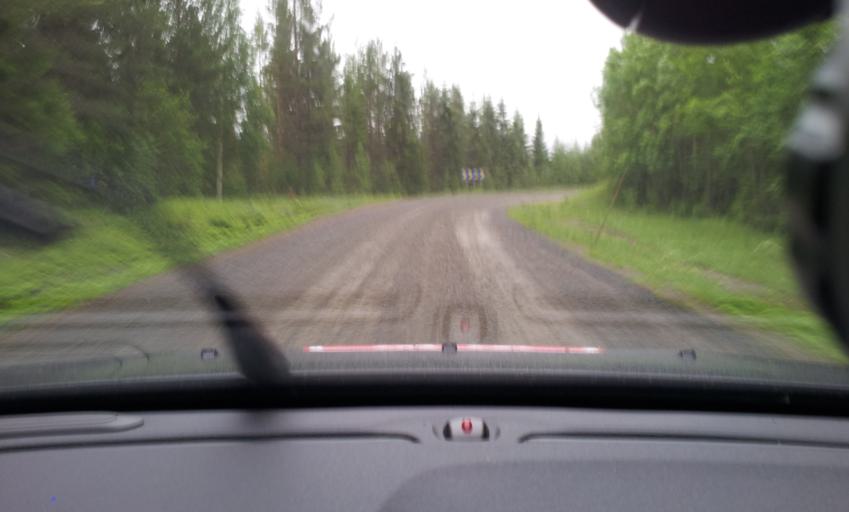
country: SE
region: Jaemtland
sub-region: Ragunda Kommun
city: Hammarstrand
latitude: 63.1356
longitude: 16.1055
